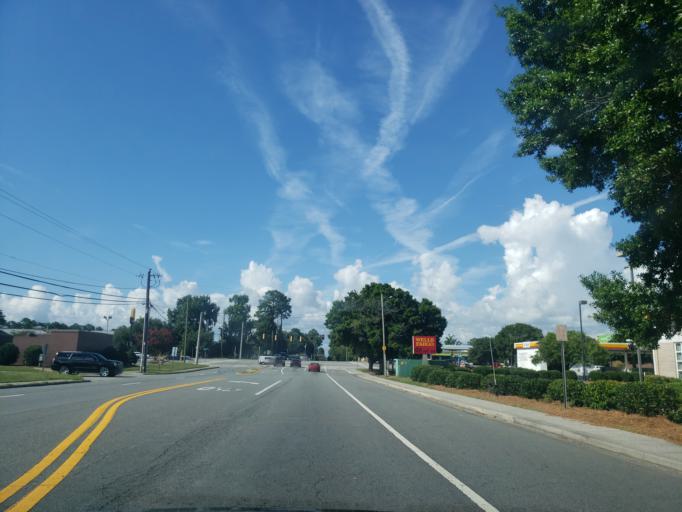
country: US
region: Georgia
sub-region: Chatham County
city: Georgetown
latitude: 31.9821
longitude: -81.1687
